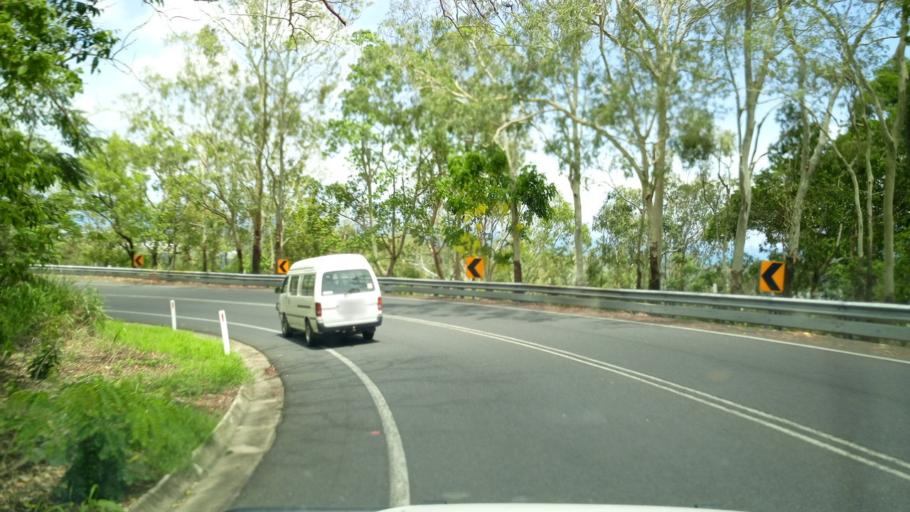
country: AU
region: Queensland
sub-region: Cairns
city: Redlynch
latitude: -16.8513
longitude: 145.6875
